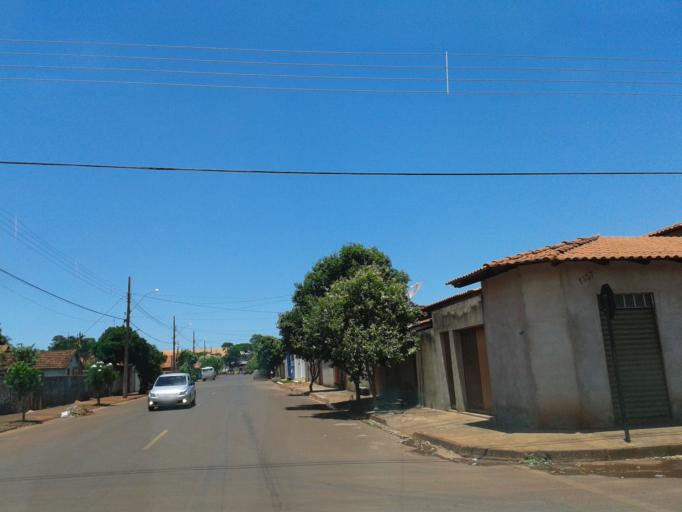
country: BR
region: Minas Gerais
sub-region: Centralina
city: Centralina
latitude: -18.7240
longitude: -49.1964
